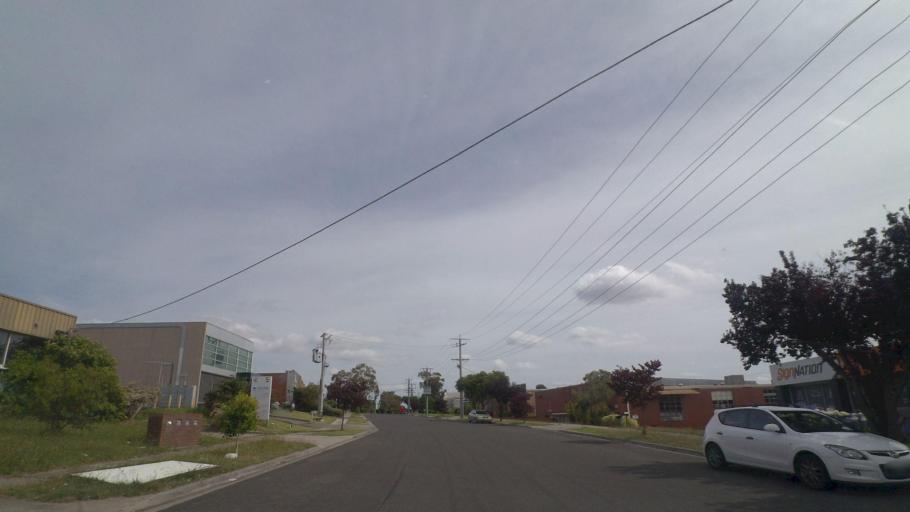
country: AU
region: Victoria
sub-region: Knox
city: Bayswater
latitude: -37.8424
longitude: 145.2817
